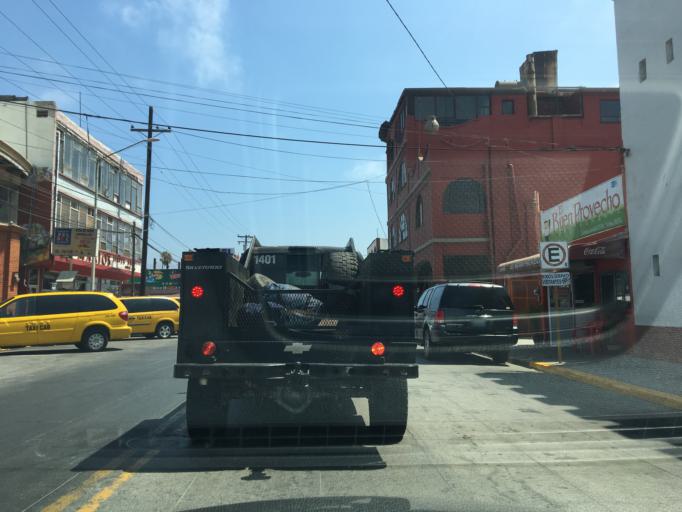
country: MX
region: Baja California
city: Ensenada
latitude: 31.8635
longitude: -116.6284
